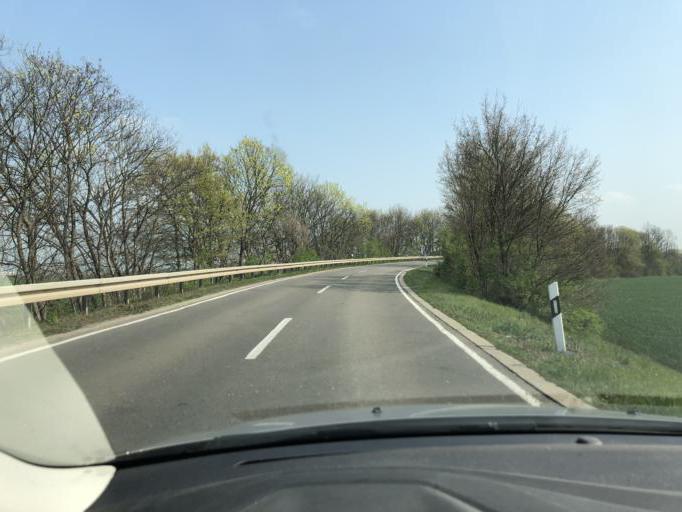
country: DE
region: Saxony-Anhalt
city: Hohenthurm
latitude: 51.5298
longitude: 12.0971
